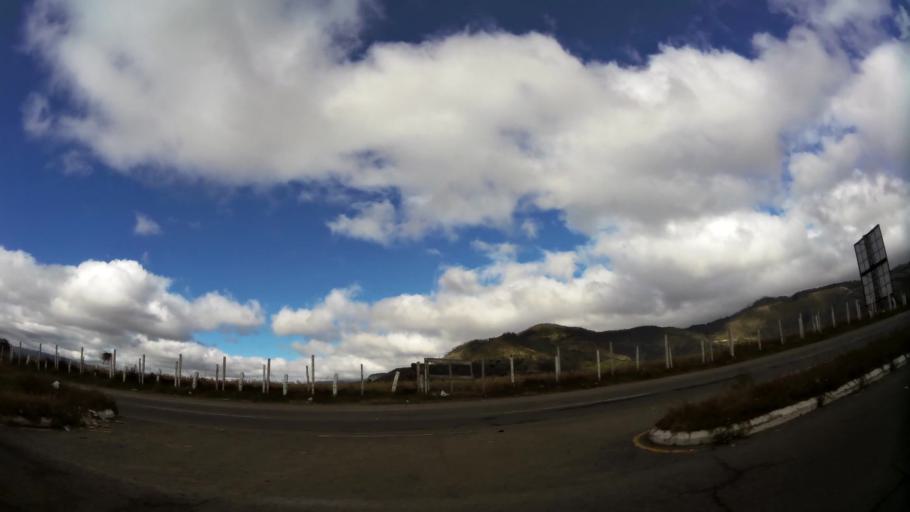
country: GT
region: Quetzaltenango
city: Salcaja
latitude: 14.8858
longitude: -91.4694
